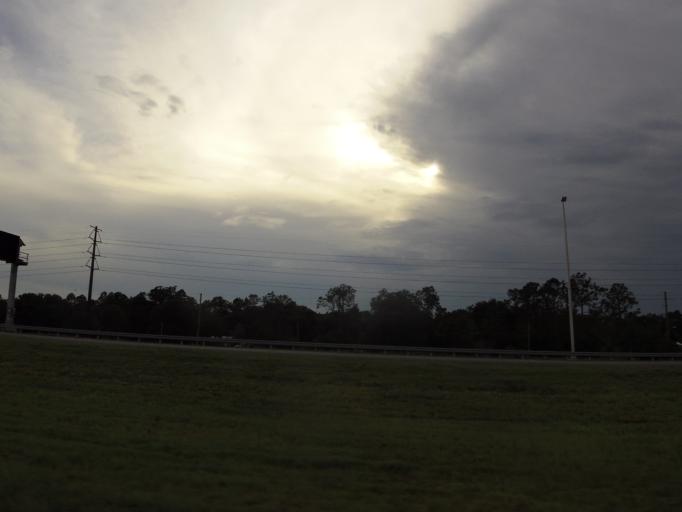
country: US
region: Florida
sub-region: Clay County
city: Lakeside
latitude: 30.1352
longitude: -81.8306
